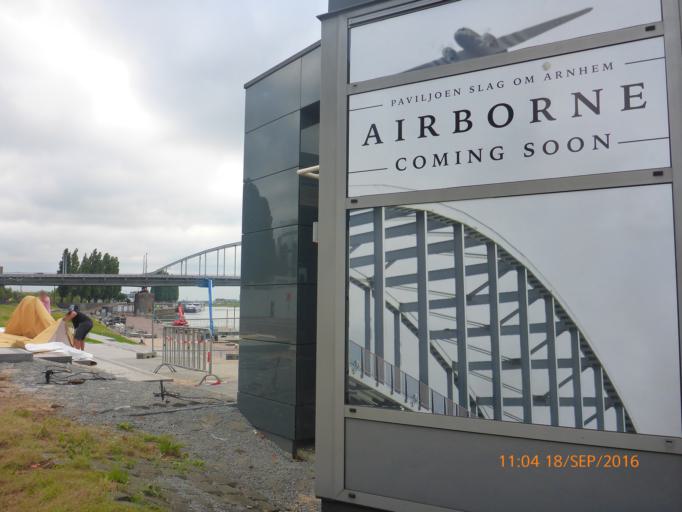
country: NL
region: Gelderland
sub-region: Gemeente Arnhem
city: Arnhem
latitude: 51.9765
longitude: 5.9093
